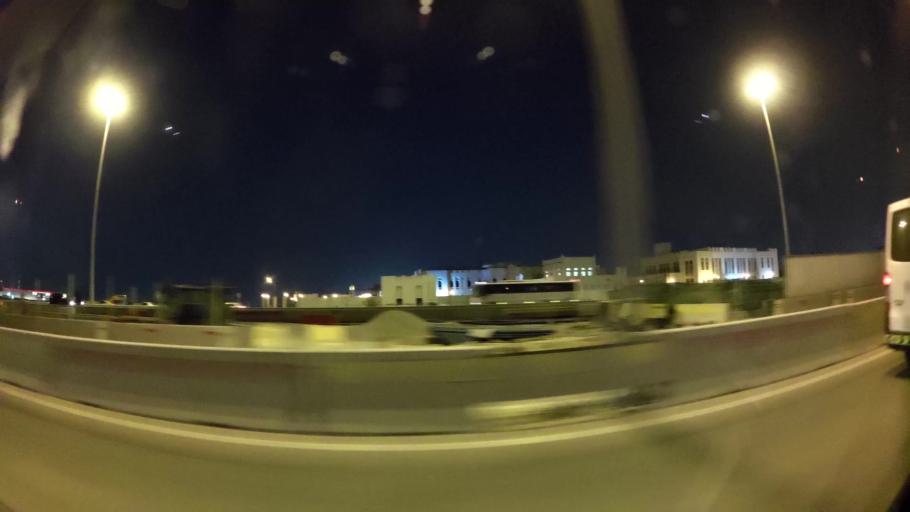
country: QA
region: Baladiyat ar Rayyan
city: Ar Rayyan
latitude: 25.2990
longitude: 51.4347
